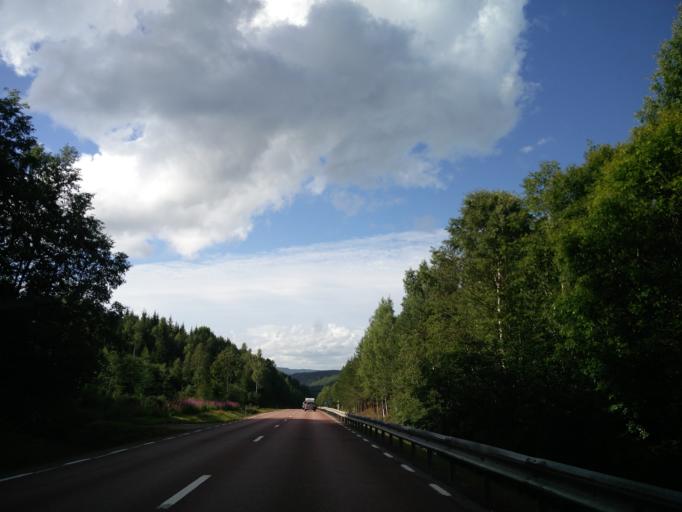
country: SE
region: Vaermland
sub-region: Hagfors Kommun
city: Ekshaerad
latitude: 60.4103
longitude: 13.2564
